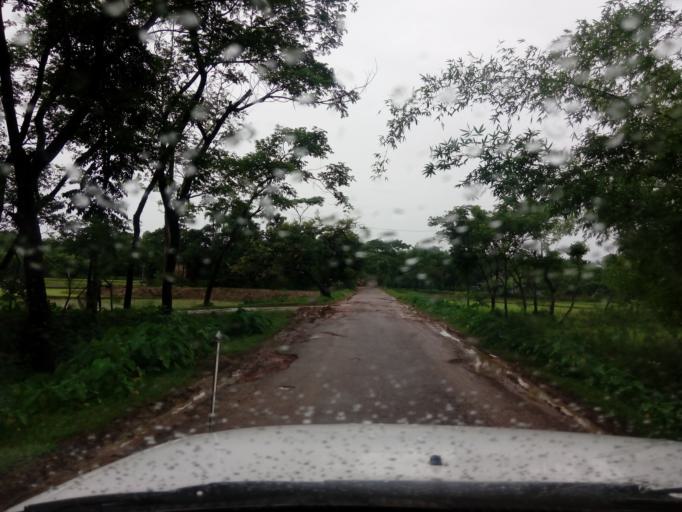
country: BD
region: Sylhet
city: Sylhet
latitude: 24.9656
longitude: 91.7931
